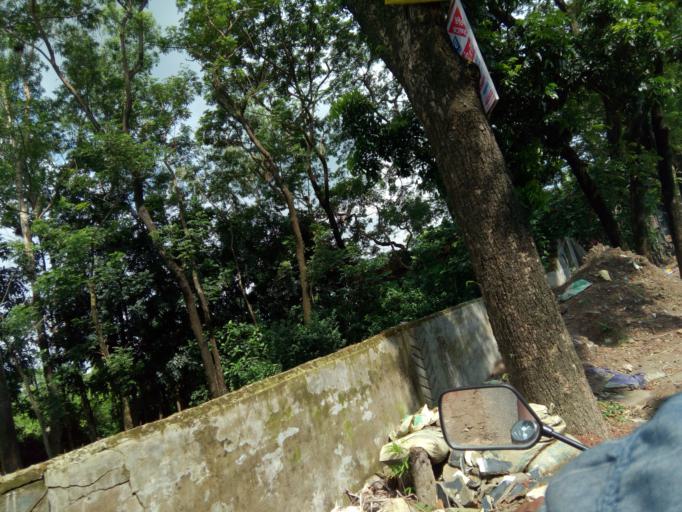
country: BD
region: Dhaka
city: Azimpur
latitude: 23.7382
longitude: 90.3335
